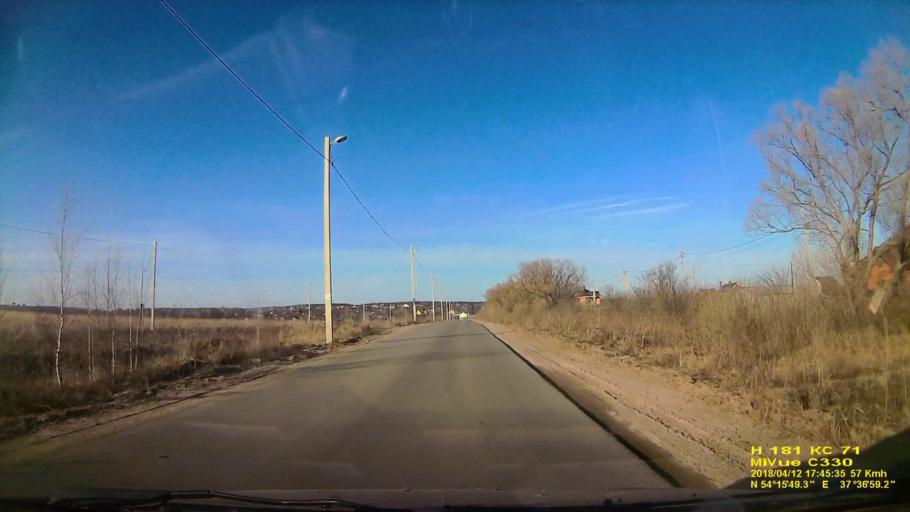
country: RU
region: Tula
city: Gorelki
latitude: 54.2638
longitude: 37.6165
